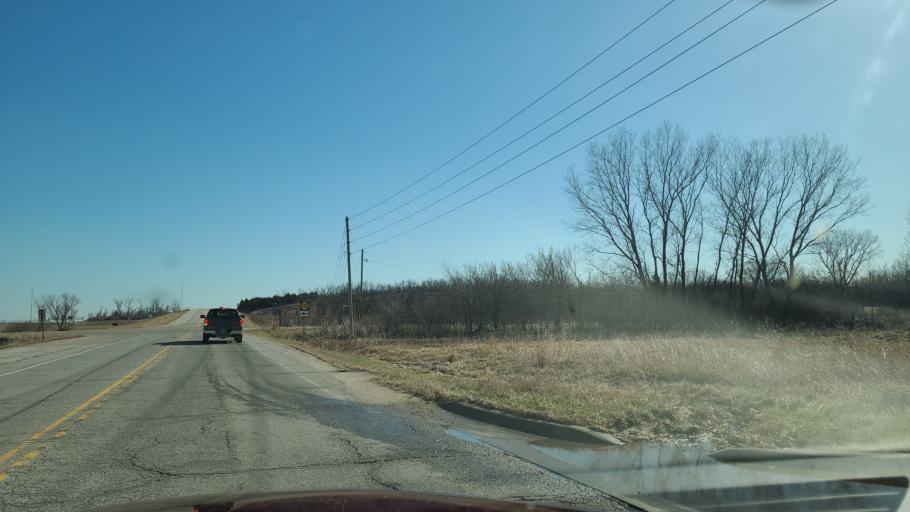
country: US
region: Kansas
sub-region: Douglas County
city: Lawrence
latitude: 38.9435
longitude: -95.1768
